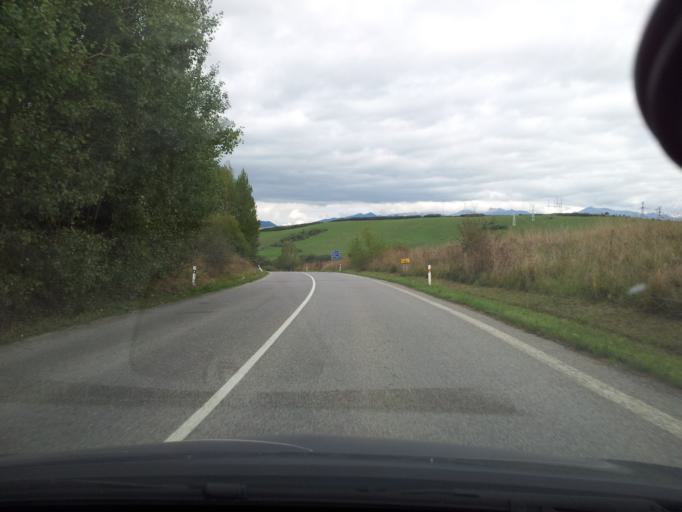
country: SK
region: Zilinsky
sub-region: Okres Liptovsky Mikulas
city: Liptovsky Mikulas
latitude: 49.0572
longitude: 19.4743
